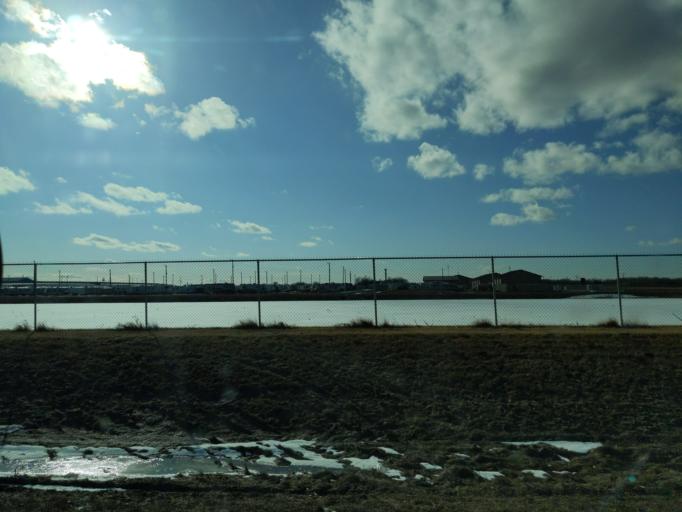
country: CA
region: Saskatchewan
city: Lloydminster
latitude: 53.2477
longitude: -109.9708
